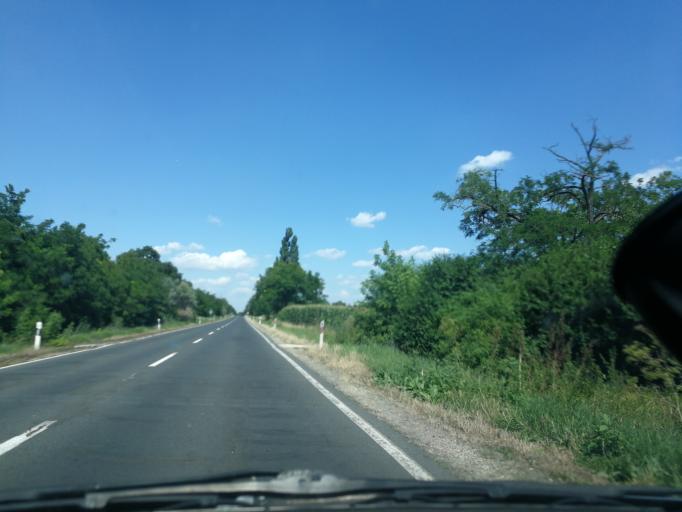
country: HU
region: Pest
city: Tarnok
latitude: 47.3423
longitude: 18.8386
